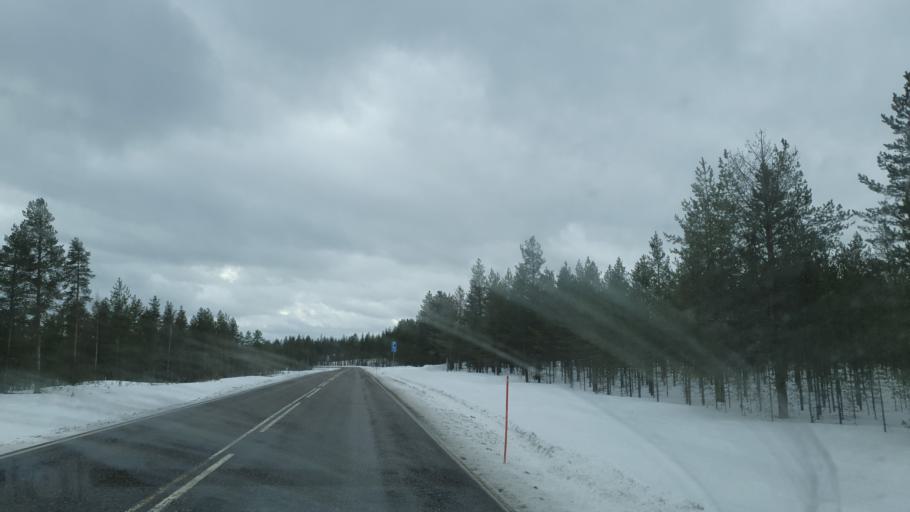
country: FI
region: Northern Ostrobothnia
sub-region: Oulunkaari
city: Pudasjaervi
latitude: 65.3634
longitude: 27.3740
